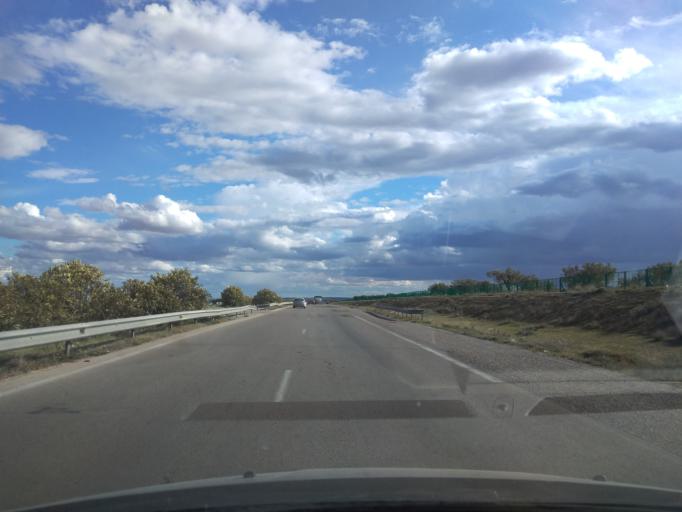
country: TN
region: Al Munastir
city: Manzil Kamil
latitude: 35.5468
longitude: 10.6207
